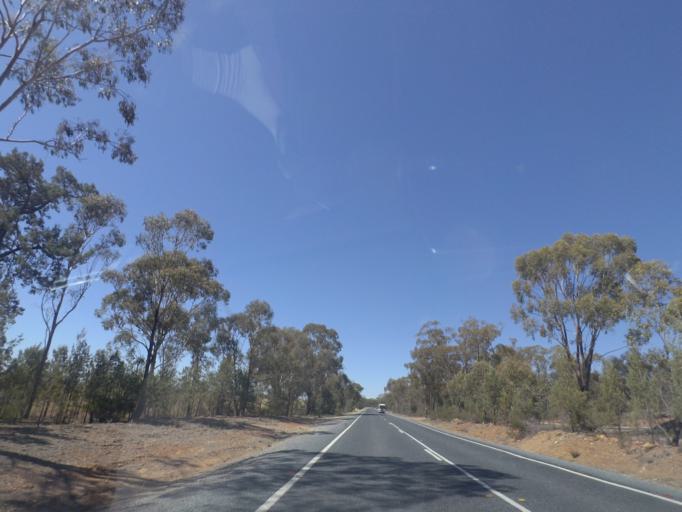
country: AU
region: New South Wales
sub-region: Narrandera
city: Narrandera
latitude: -34.4357
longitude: 146.8423
